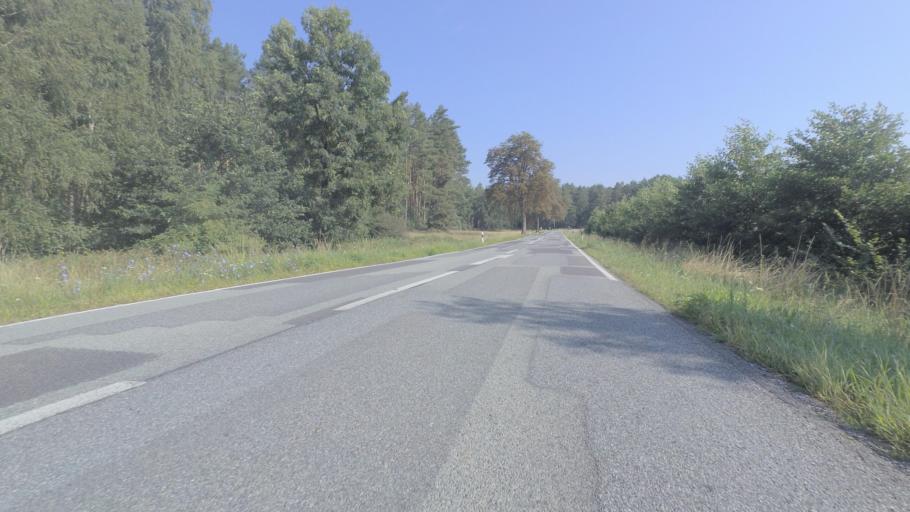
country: DE
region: Mecklenburg-Vorpommern
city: Malchow
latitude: 53.5439
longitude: 12.4335
